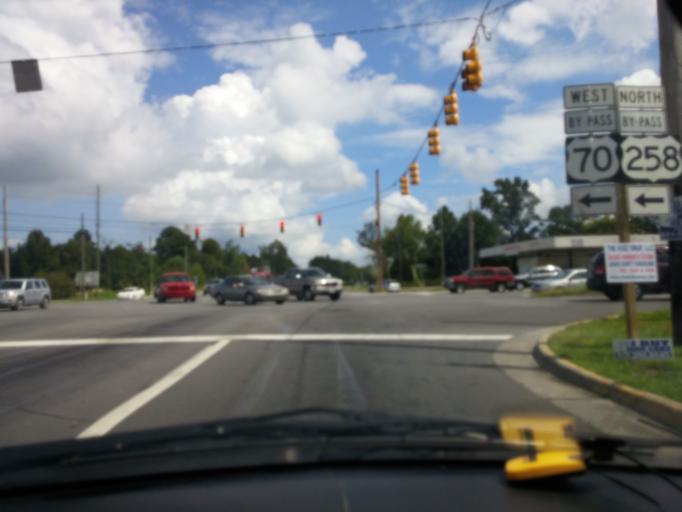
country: US
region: North Carolina
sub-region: Lenoir County
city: Kinston
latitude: 35.2542
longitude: -77.6019
